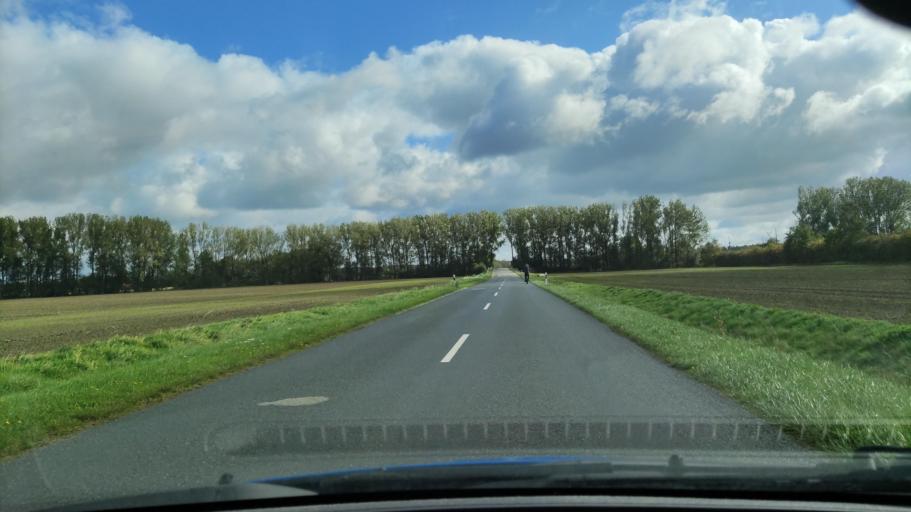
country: DE
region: Saxony-Anhalt
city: Salzwedel
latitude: 52.8539
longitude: 11.1950
